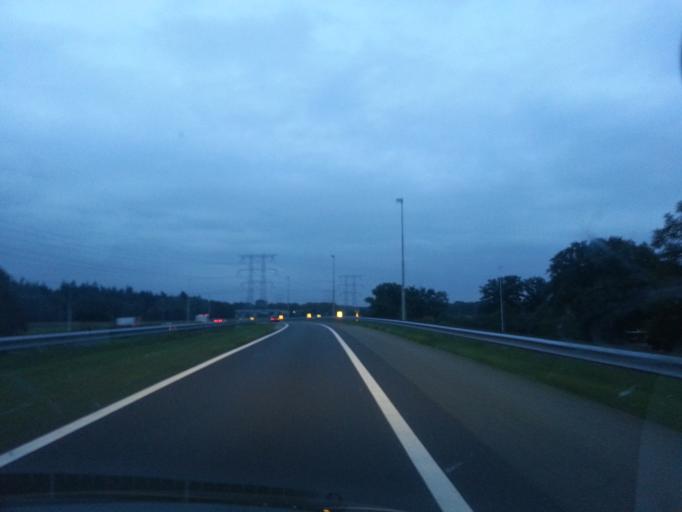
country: NL
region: North Brabant
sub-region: Gemeente Tilburg
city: Tilburg
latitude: 51.5519
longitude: 5.1296
